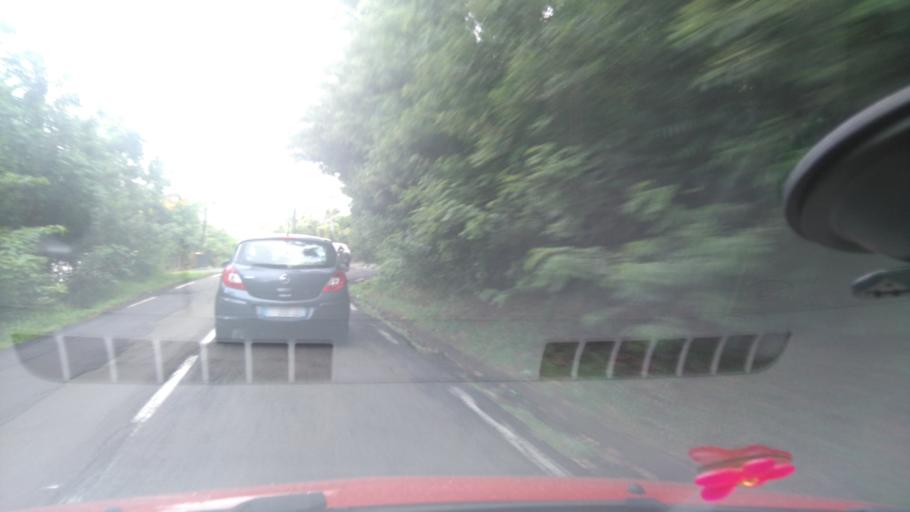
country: MQ
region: Martinique
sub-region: Martinique
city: Saint-Esprit
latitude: 14.5537
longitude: -60.9558
